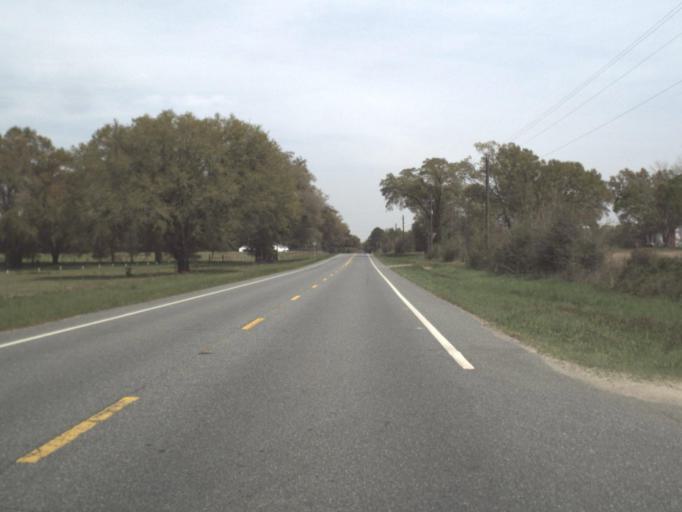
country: US
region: Florida
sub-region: Jackson County
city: Malone
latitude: 30.9570
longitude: -85.1476
